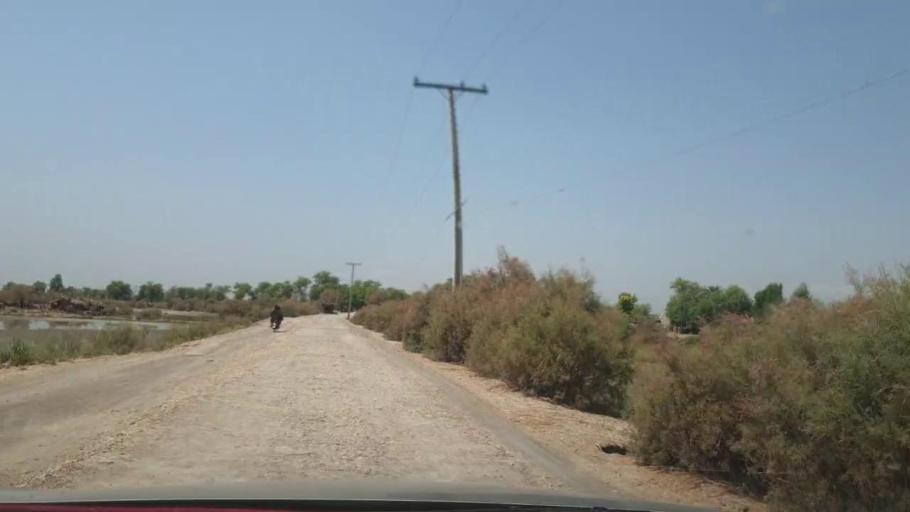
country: PK
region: Sindh
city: Warah
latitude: 27.4839
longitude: 67.7343
